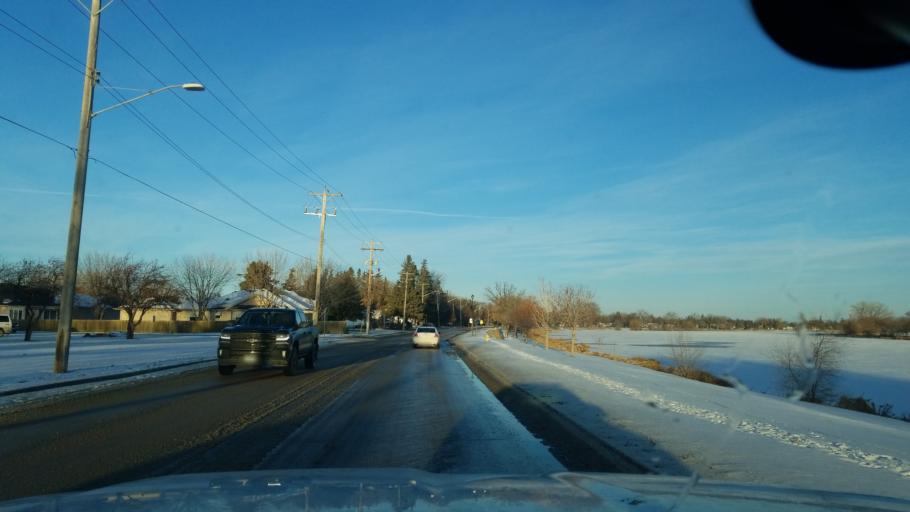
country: CA
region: Manitoba
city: Portage la Prairie
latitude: 49.9660
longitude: -98.3194
